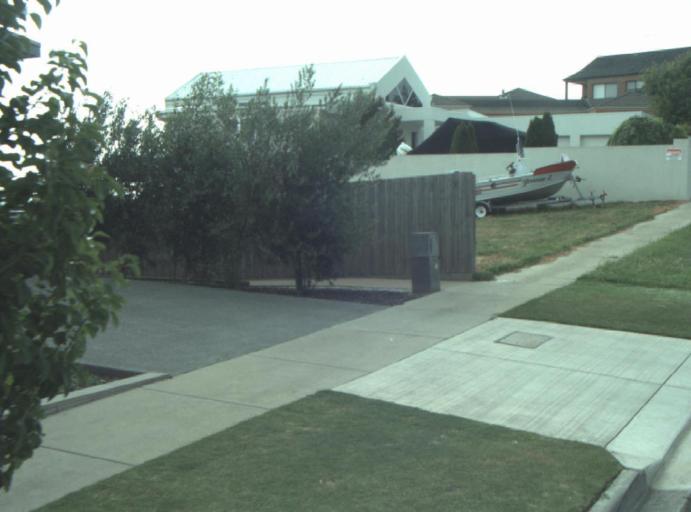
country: AU
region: Victoria
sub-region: Greater Geelong
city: Wandana Heights
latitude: -38.1540
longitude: 144.3171
